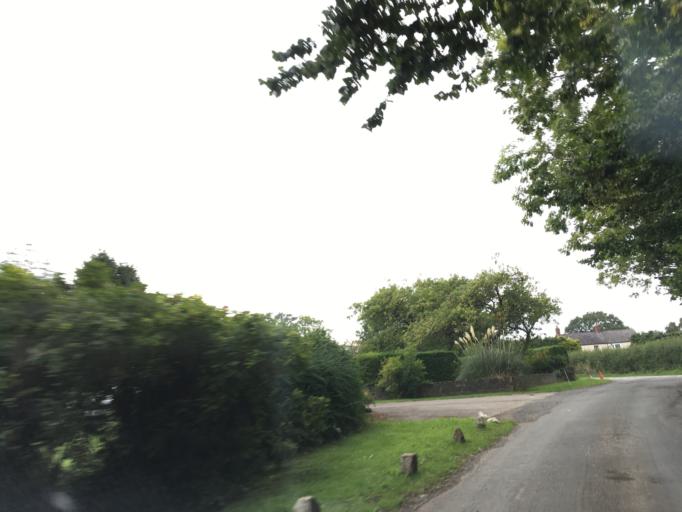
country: GB
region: England
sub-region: South Gloucestershire
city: Falfield
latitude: 51.6489
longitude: -2.4757
